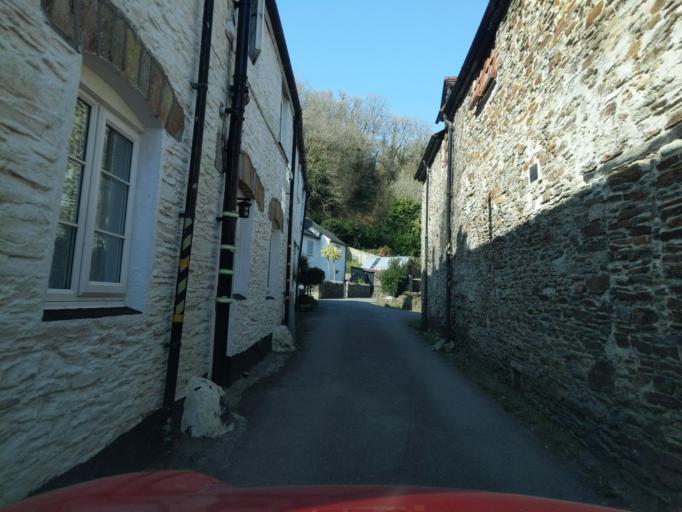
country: GB
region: England
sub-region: Devon
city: Horrabridge
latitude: 50.4732
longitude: -4.1319
